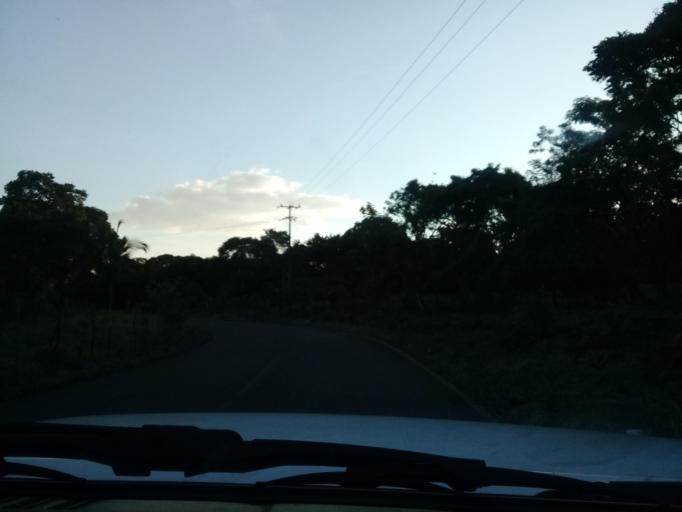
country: MX
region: Veracruz
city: Catemaco
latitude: 18.4281
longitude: -95.0945
